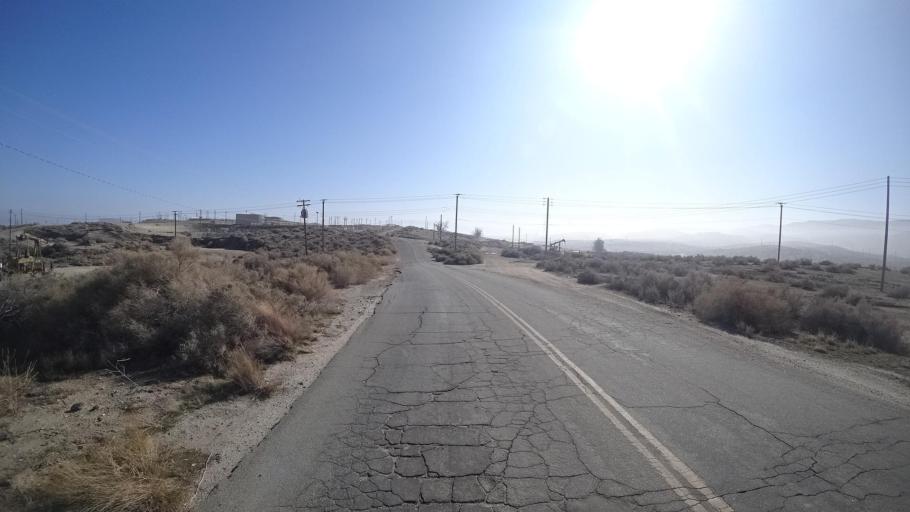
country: US
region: California
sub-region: Kern County
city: Taft Heights
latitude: 35.1169
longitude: -119.4779
